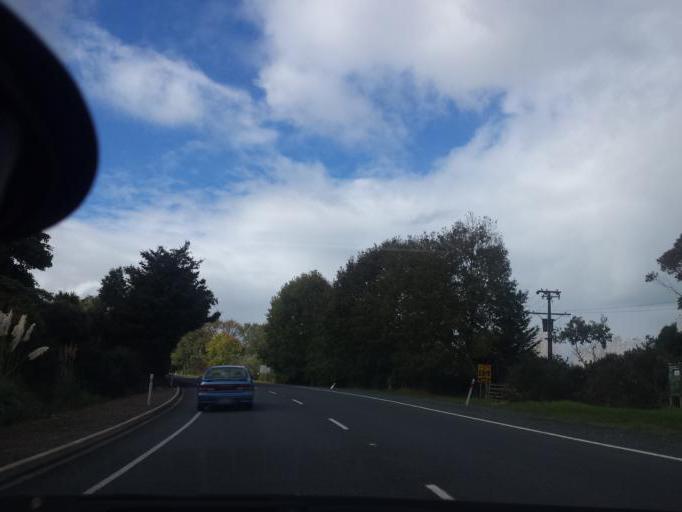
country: NZ
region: Auckland
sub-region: Auckland
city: Warkworth
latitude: -36.3986
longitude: 174.7038
